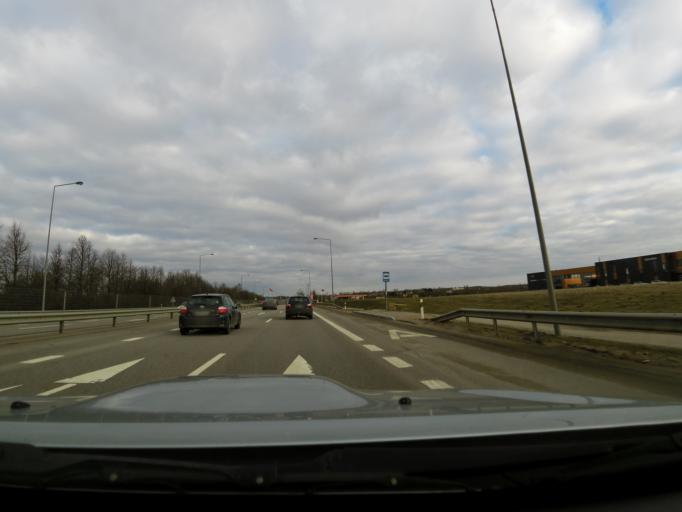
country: LT
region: Vilnius County
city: Pasilaiciai
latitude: 54.7506
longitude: 25.2141
